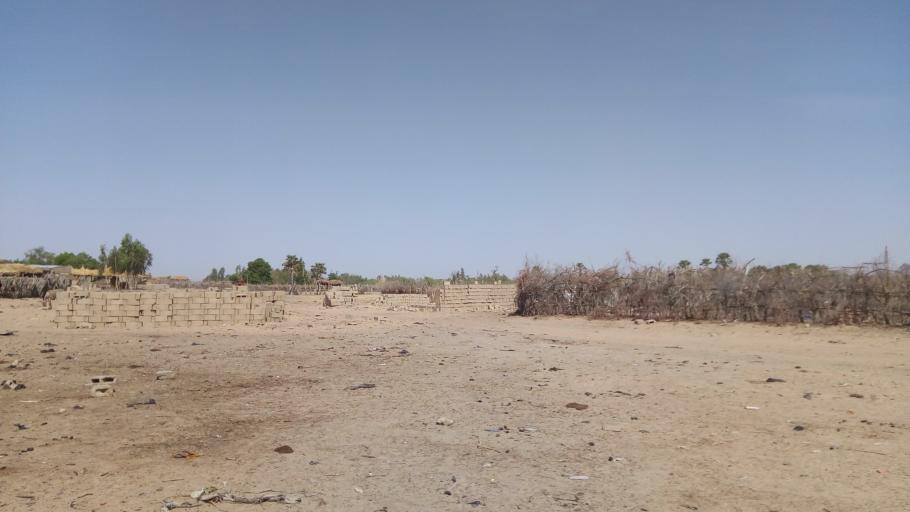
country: ML
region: Kayes
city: Diema
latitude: 14.5138
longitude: -8.8409
